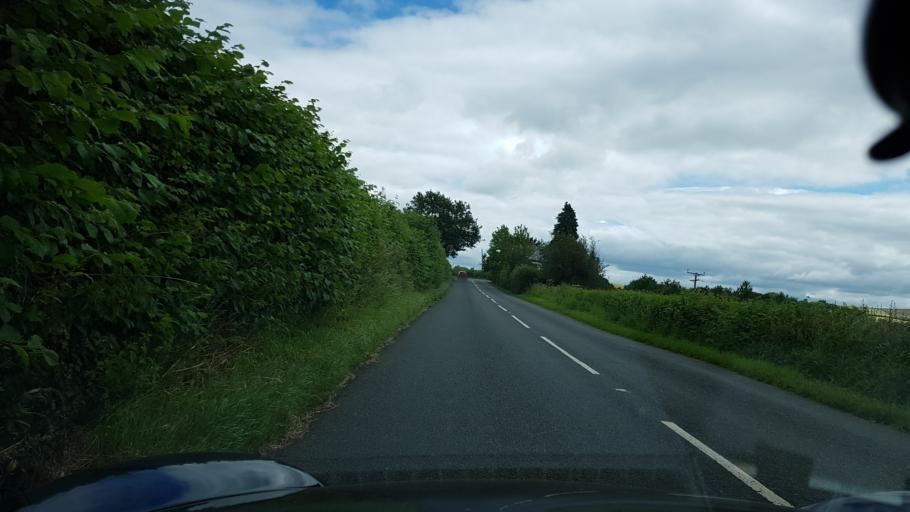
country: GB
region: Wales
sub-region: Monmouthshire
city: Grosmont
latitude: 51.8604
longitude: -2.8900
